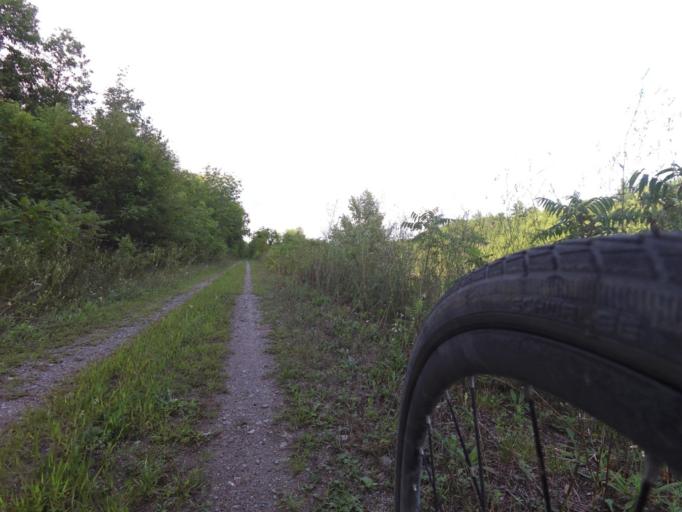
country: CA
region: Ontario
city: Kingston
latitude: 44.5272
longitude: -76.4090
